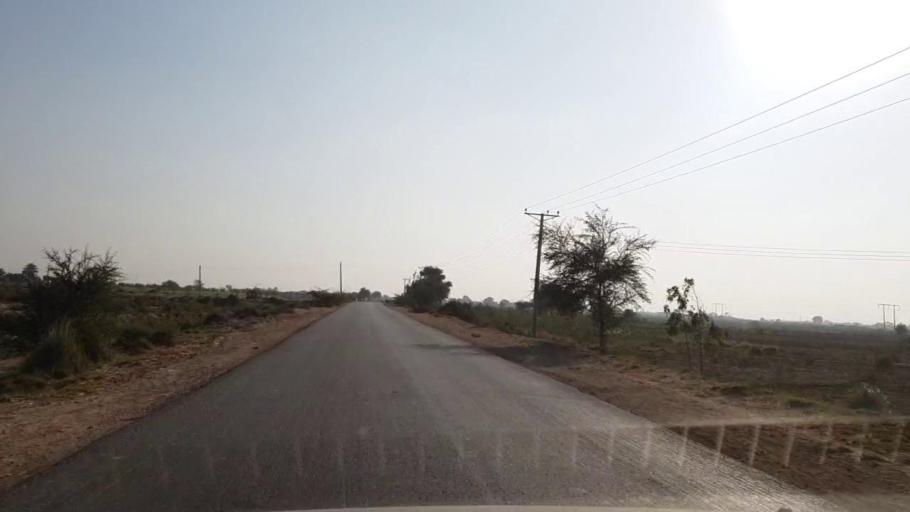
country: PK
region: Sindh
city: Bulri
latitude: 24.8980
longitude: 68.3456
